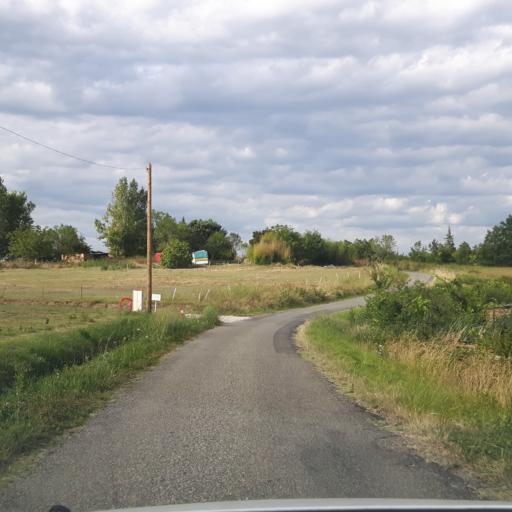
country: FR
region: Midi-Pyrenees
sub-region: Departement de la Haute-Garonne
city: Castelnau-d'Estretefonds
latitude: 43.7872
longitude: 1.3737
